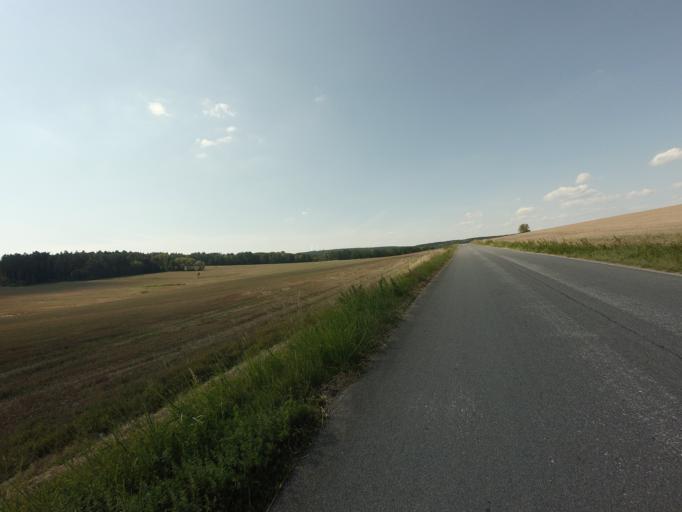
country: CZ
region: Jihocesky
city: Tyn nad Vltavou
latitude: 49.1434
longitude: 14.4468
